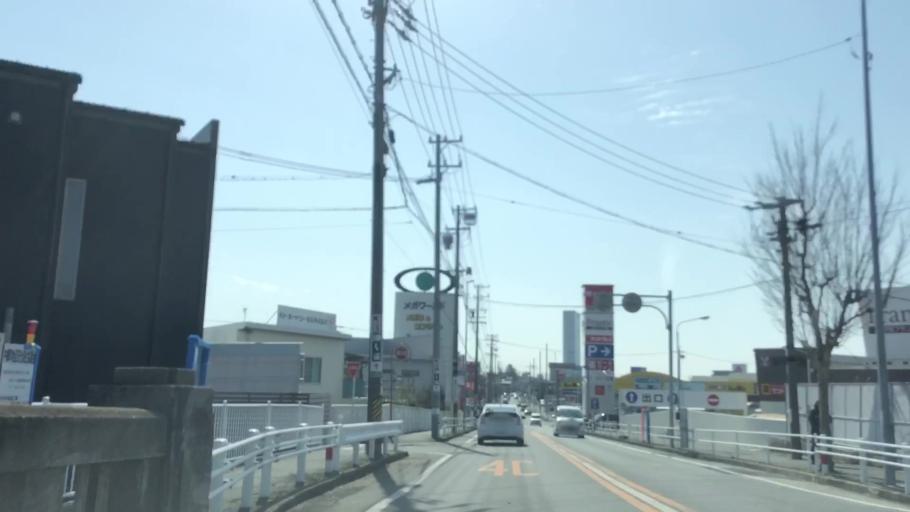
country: JP
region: Aichi
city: Toyohashi
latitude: 34.7529
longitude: 137.3788
